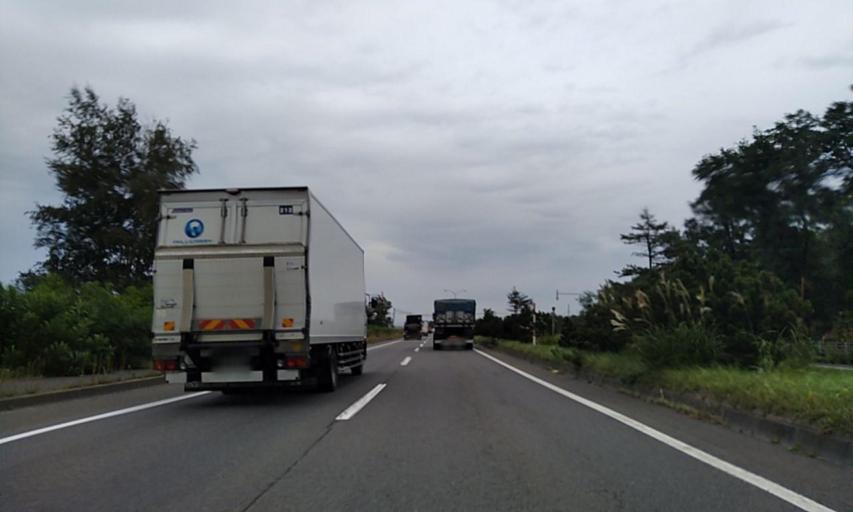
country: JP
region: Hokkaido
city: Sapporo
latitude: 43.1545
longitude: 141.2411
